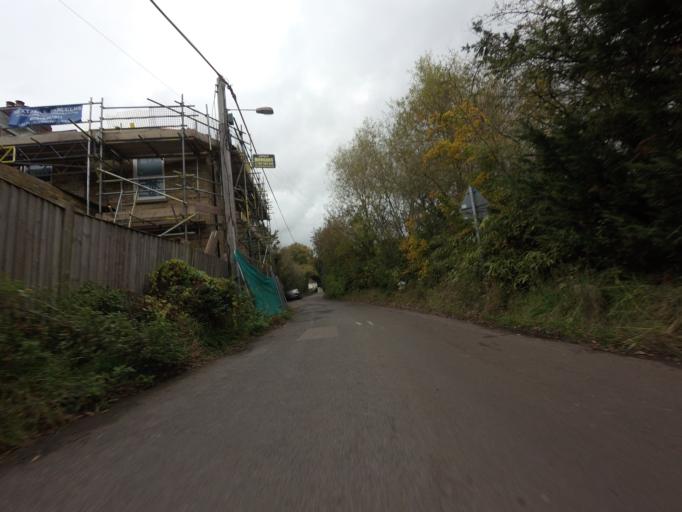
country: GB
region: England
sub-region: Kent
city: Swanley
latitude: 51.3861
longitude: 0.1602
